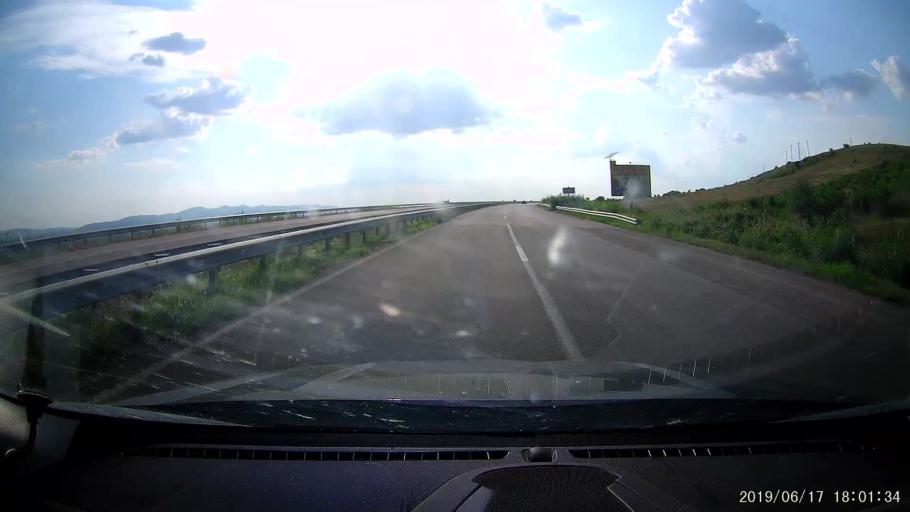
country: BG
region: Khaskovo
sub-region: Obshtina Svilengrad
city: Svilengrad
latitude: 41.7463
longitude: 26.2508
